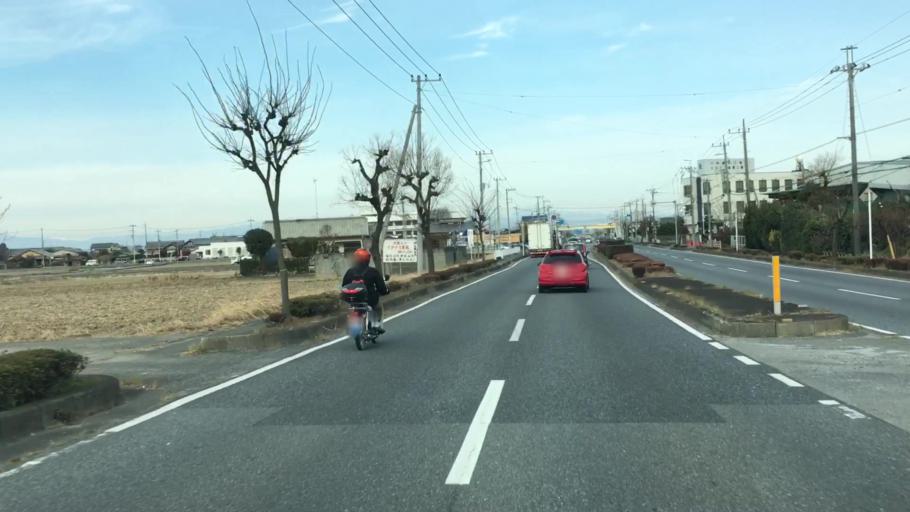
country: JP
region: Saitama
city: Menuma
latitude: 36.2204
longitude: 139.3683
